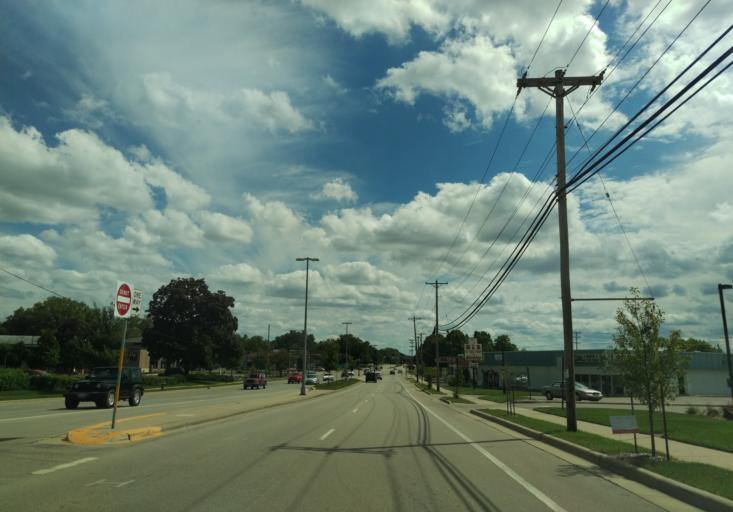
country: US
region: Wisconsin
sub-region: Dane County
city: Maple Bluff
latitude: 43.1346
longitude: -89.3729
